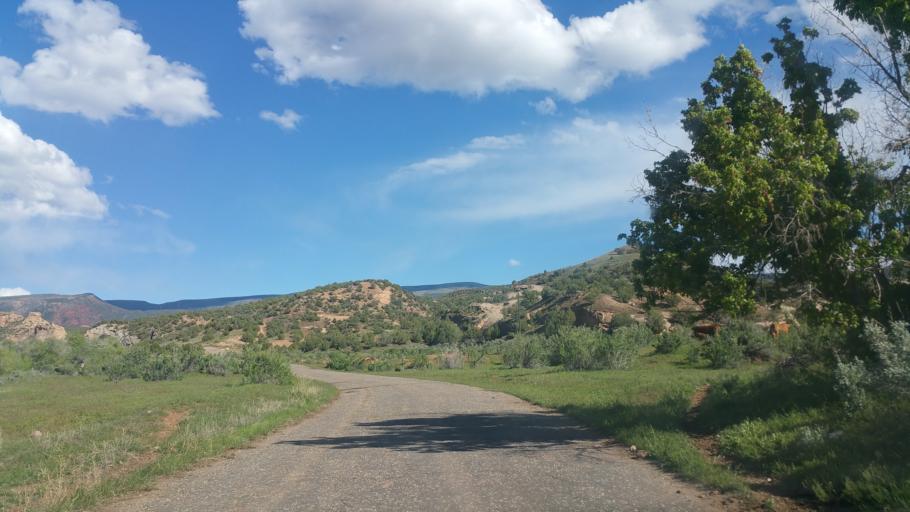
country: US
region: Utah
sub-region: Uintah County
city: Naples
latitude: 40.4211
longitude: -109.2053
